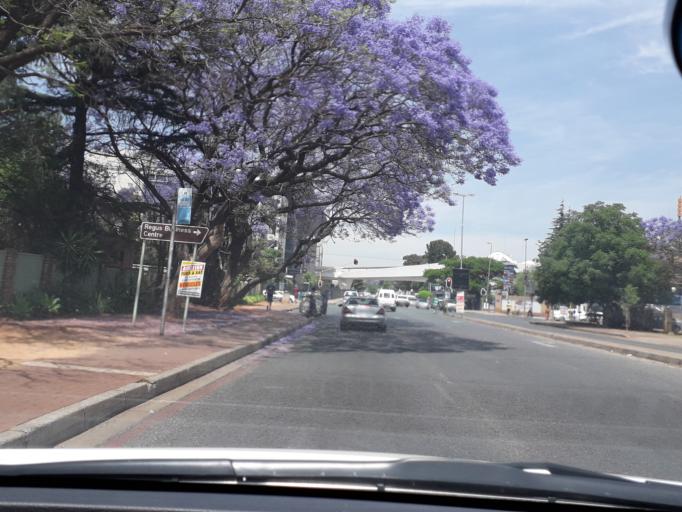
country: ZA
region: Gauteng
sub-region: City of Johannesburg Metropolitan Municipality
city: Johannesburg
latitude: -26.0995
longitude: 28.0030
